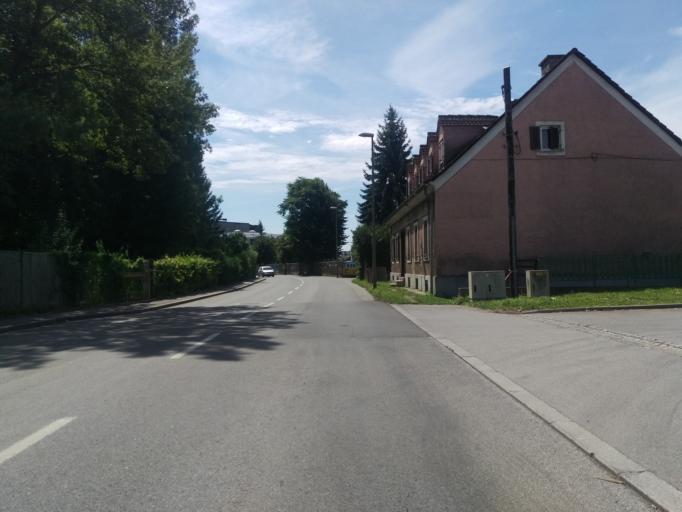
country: AT
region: Styria
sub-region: Graz Stadt
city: Graz
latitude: 47.0475
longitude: 15.4348
